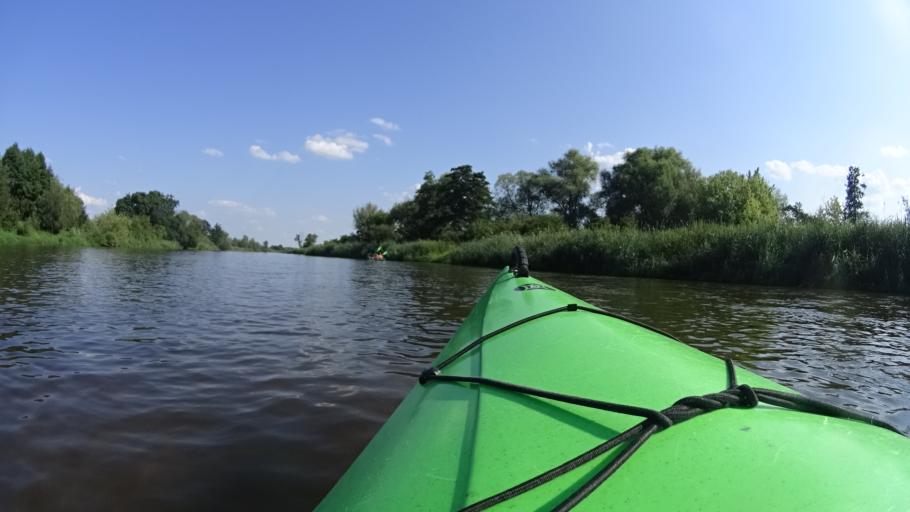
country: PL
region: Masovian Voivodeship
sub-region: Powiat bialobrzeski
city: Bialobrzegi
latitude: 51.6642
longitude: 20.9226
